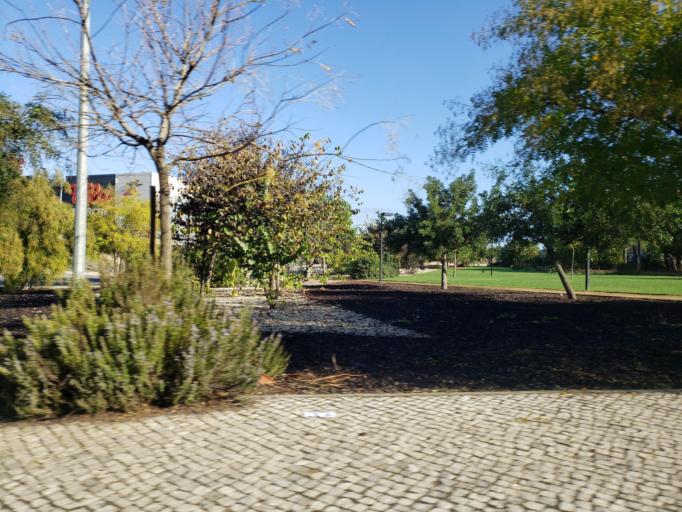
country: PT
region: Faro
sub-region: Portimao
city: Portimao
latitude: 37.1517
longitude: -8.5544
